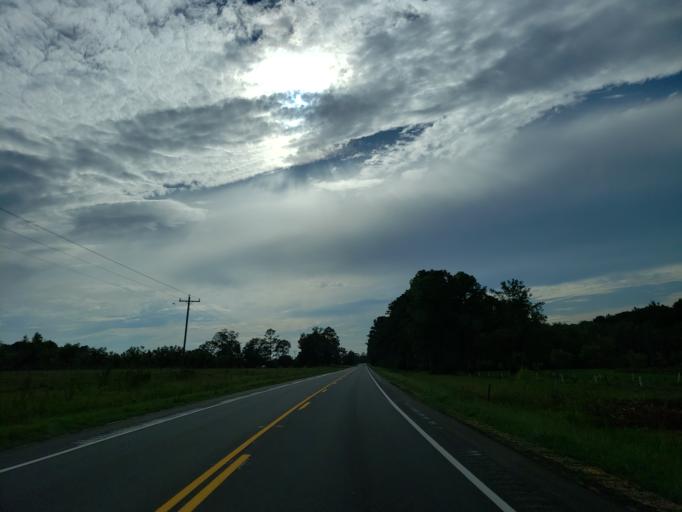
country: US
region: Georgia
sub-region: Irwin County
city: Ocilla
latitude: 31.5632
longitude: -83.3289
